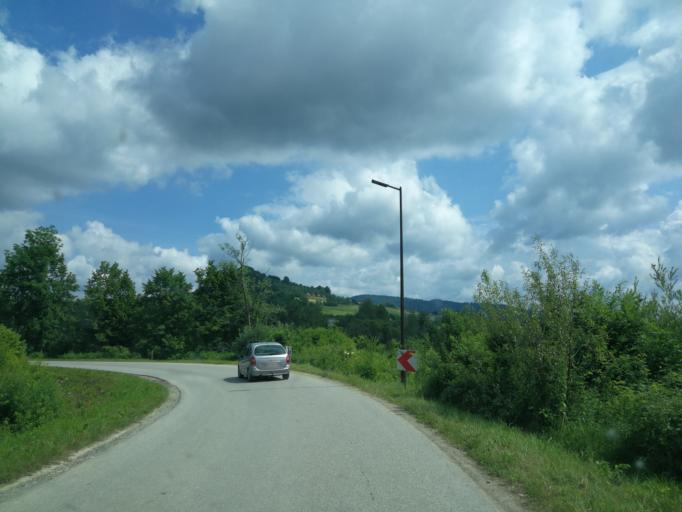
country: PL
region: Subcarpathian Voivodeship
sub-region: Powiat leski
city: Polanczyk
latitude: 49.4154
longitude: 22.4430
